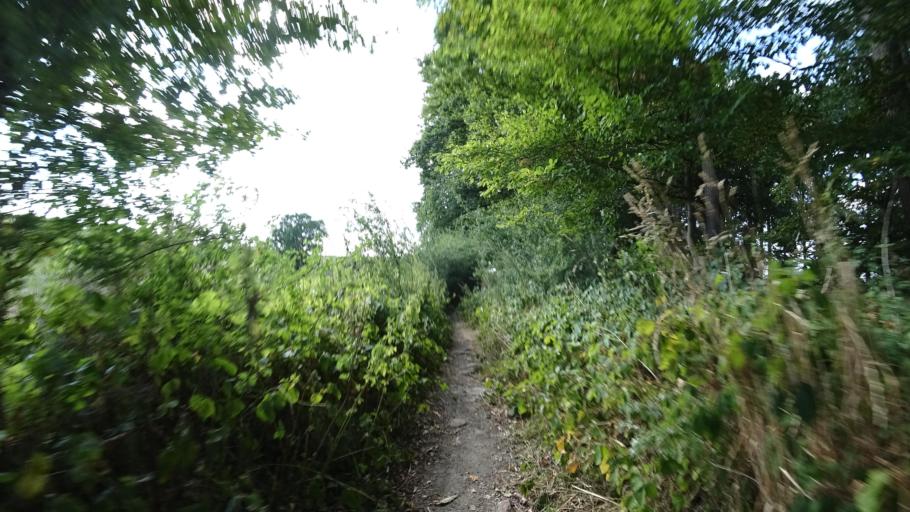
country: DE
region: North Rhine-Westphalia
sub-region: Regierungsbezirk Detmold
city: Rheda-Wiedenbruck
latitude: 51.8314
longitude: 8.2848
